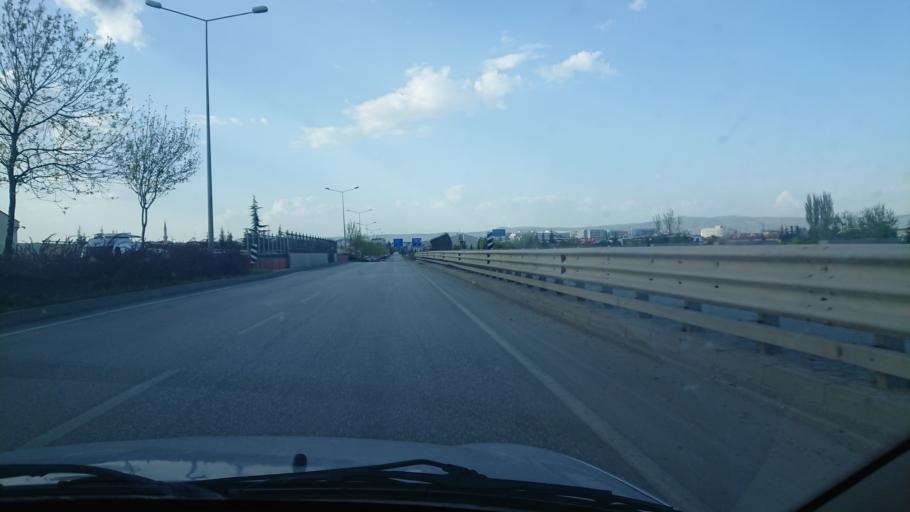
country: TR
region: Eskisehir
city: Eskisehir
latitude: 39.7752
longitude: 30.4840
